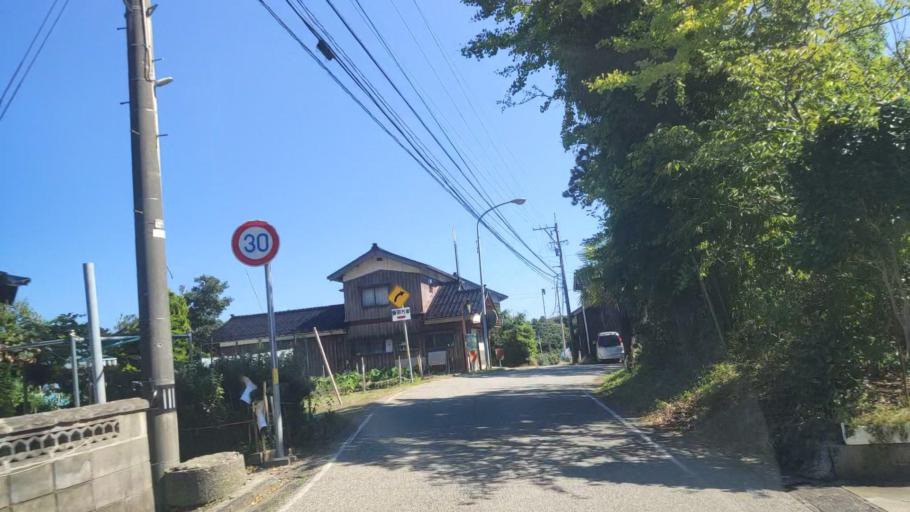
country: JP
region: Toyama
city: Nyuzen
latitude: 37.5048
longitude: 137.3481
